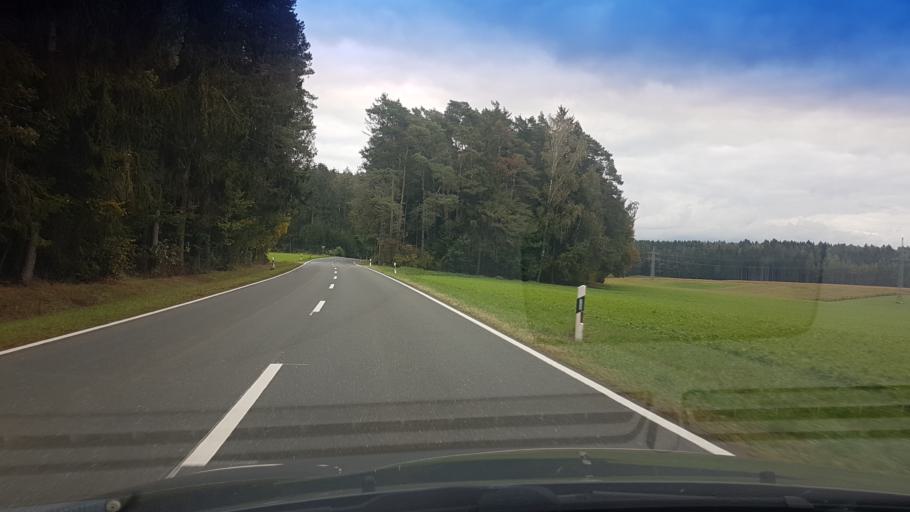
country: DE
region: Bavaria
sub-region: Upper Franconia
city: Stadelhofen
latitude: 50.0106
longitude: 11.2103
